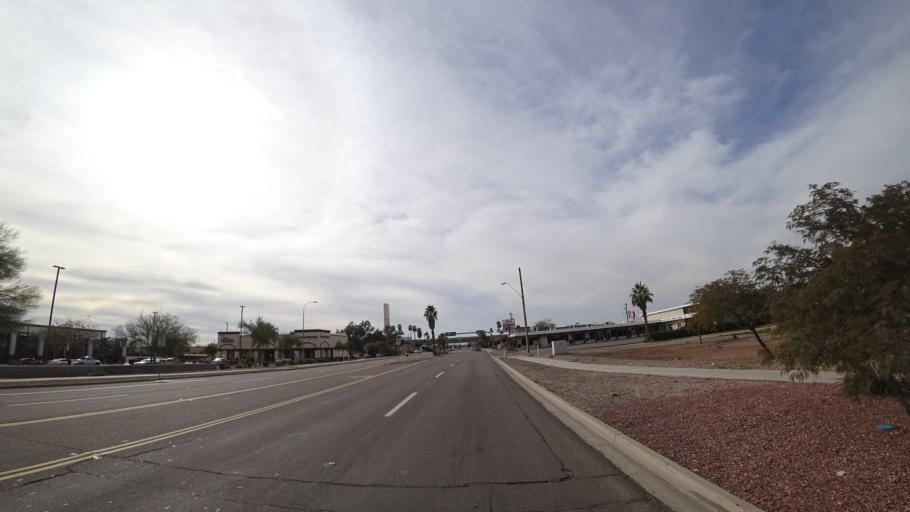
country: US
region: Arizona
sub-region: Maricopa County
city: Peoria
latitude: 33.5808
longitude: -112.2565
